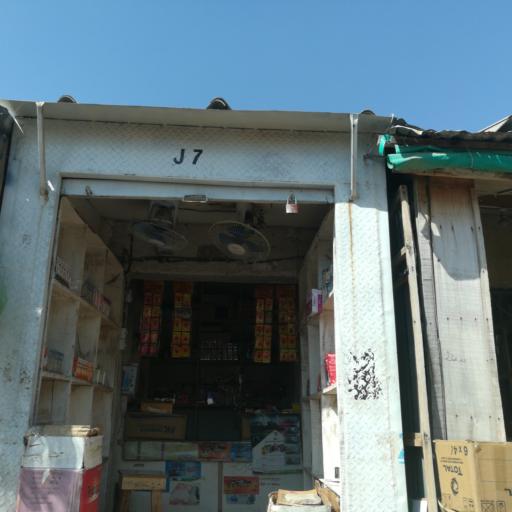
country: NG
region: Kano
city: Kano
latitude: 12.0117
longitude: 8.5354
